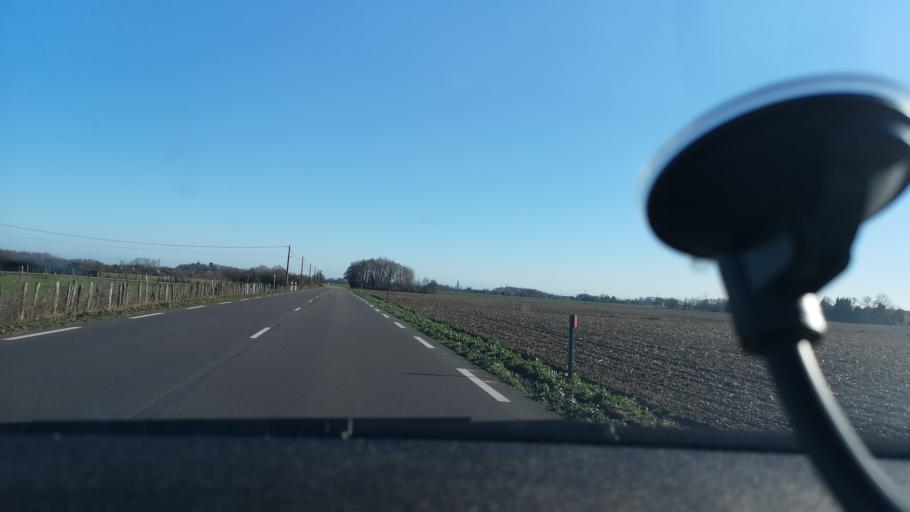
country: FR
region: Bourgogne
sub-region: Departement de Saone-et-Loire
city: Saint-Martin-en-Bresse
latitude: 46.7446
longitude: 5.0645
